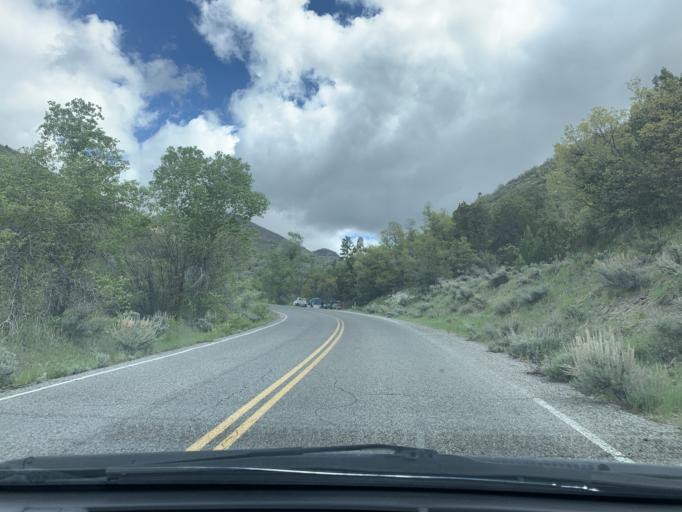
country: US
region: Utah
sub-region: Juab County
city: Nephi
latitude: 39.7667
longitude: -111.7063
